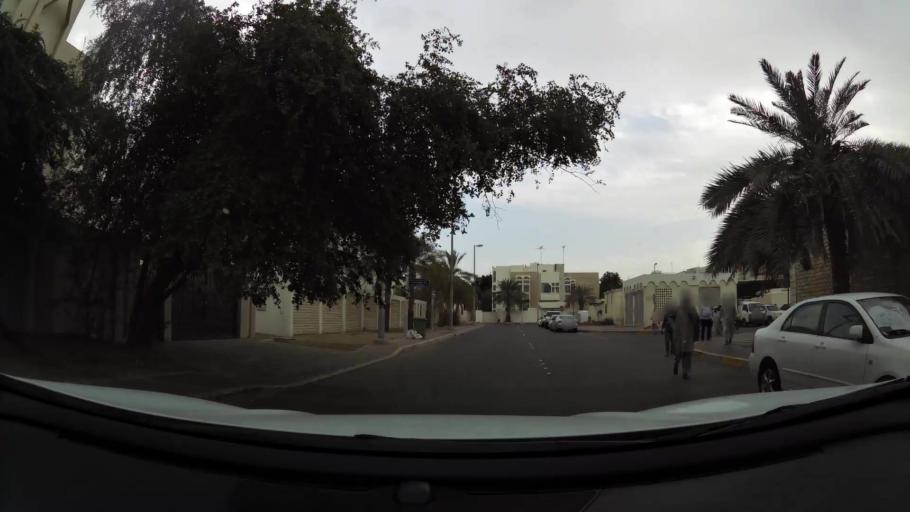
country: AE
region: Abu Dhabi
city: Abu Dhabi
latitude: 24.4801
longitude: 54.3735
